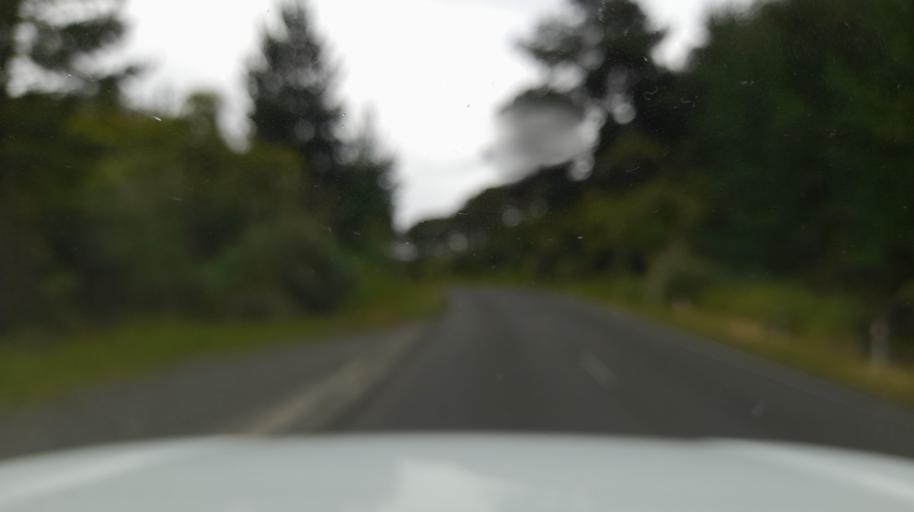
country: NZ
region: Northland
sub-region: Far North District
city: Kaitaia
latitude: -35.2752
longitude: 173.3117
